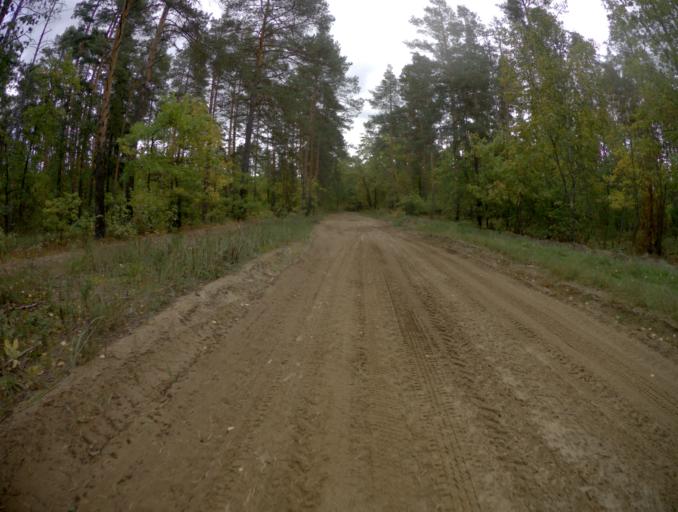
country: RU
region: Vladimir
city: Petushki
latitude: 55.8859
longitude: 39.5120
